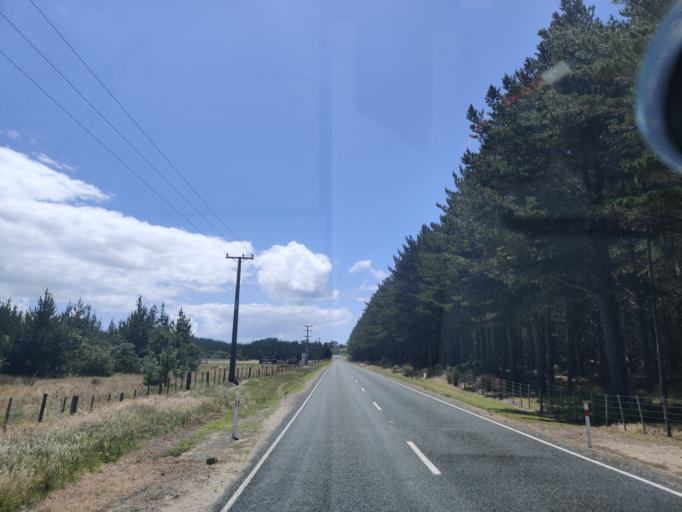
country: NZ
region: Northland
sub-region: Far North District
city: Kaitaia
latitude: -35.0364
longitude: 173.1762
